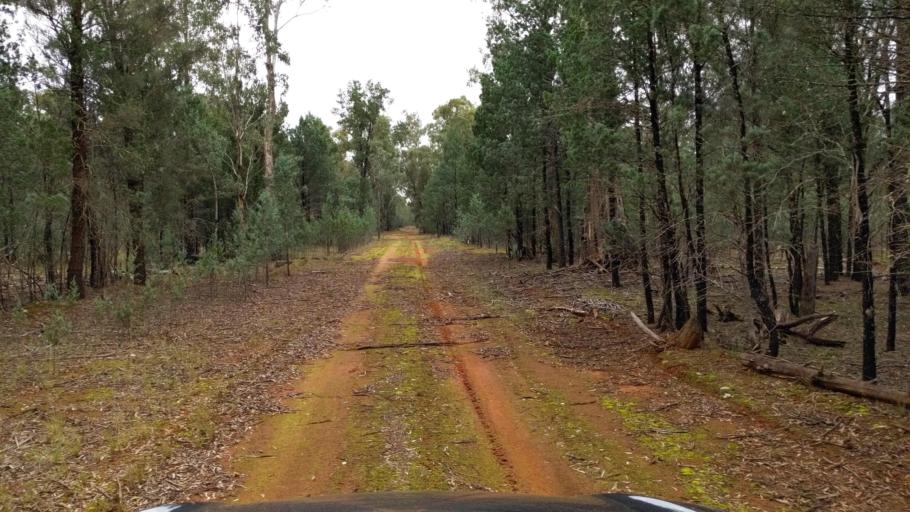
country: AU
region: New South Wales
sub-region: Coolamon
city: Coolamon
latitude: -34.8402
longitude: 146.9338
